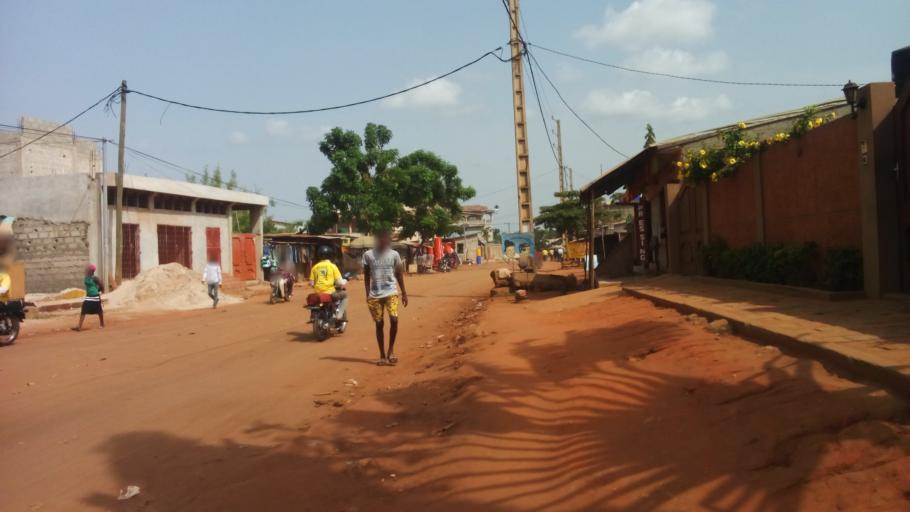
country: BJ
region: Atlantique
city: Abomey-Calavi
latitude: 6.4248
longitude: 2.3199
